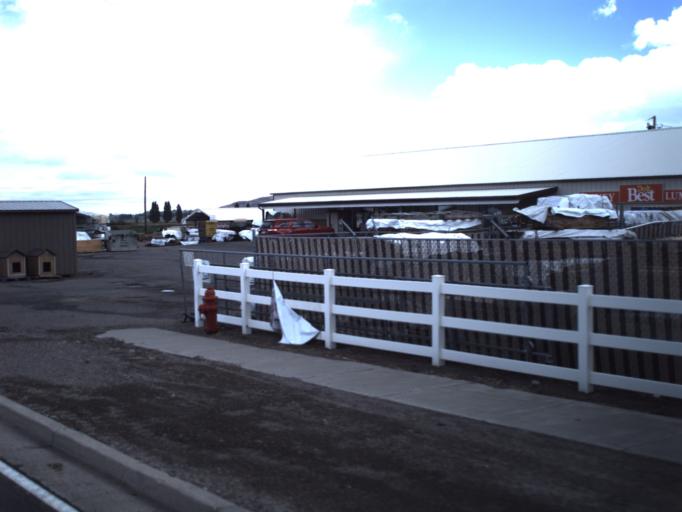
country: US
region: Utah
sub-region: Sevier County
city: Monroe
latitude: 38.6400
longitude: -112.1214
